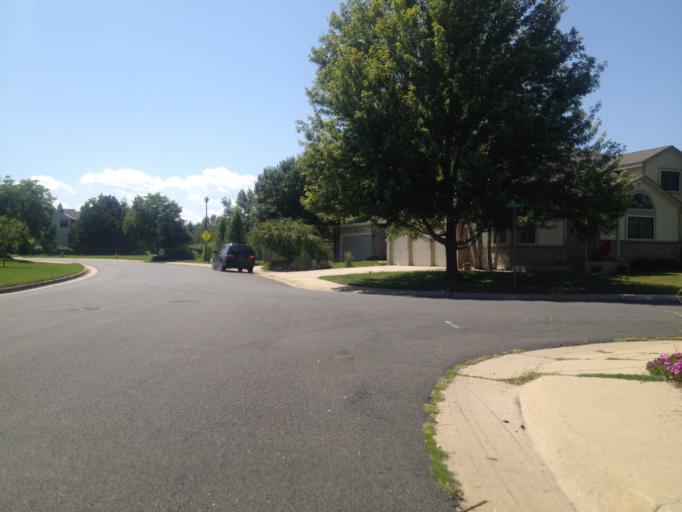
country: US
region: Colorado
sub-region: Boulder County
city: Superior
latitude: 39.9583
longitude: -105.1471
